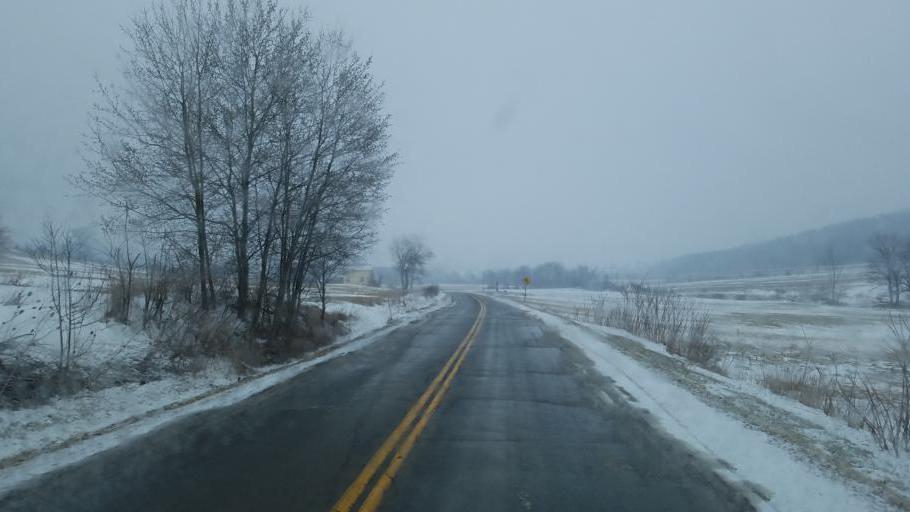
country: US
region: New York
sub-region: Steuben County
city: Canisteo
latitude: 42.1367
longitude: -77.5421
